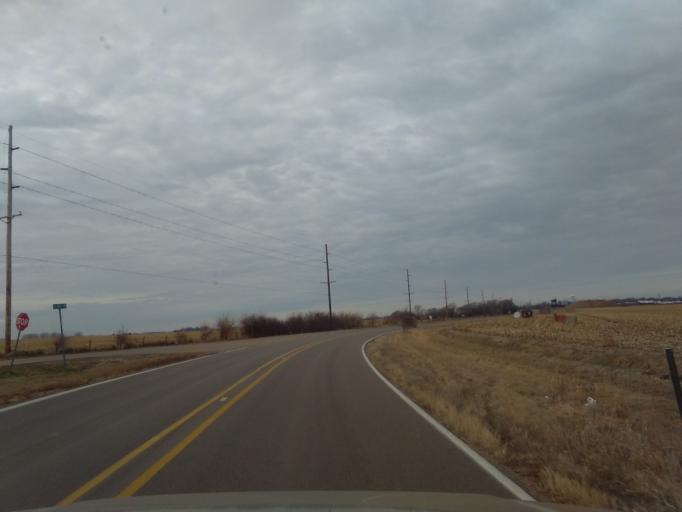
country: US
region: Nebraska
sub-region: Hall County
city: Grand Island
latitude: 40.7713
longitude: -98.3427
